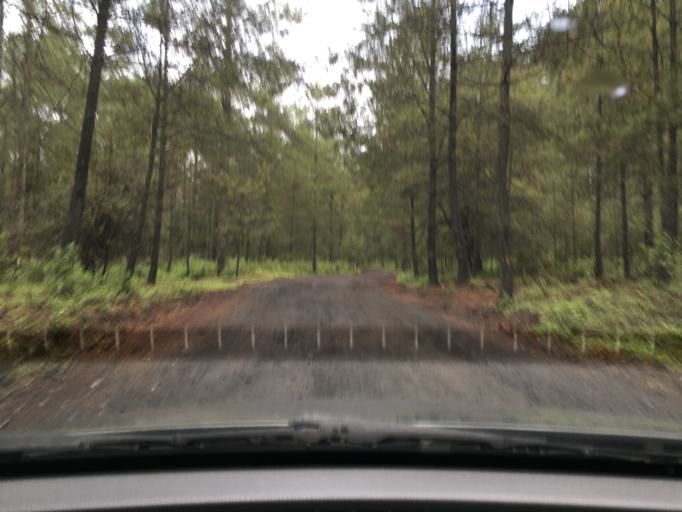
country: MX
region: Michoacan
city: Nuevo San Juan Parangaricutiro
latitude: 19.4577
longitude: -102.1893
